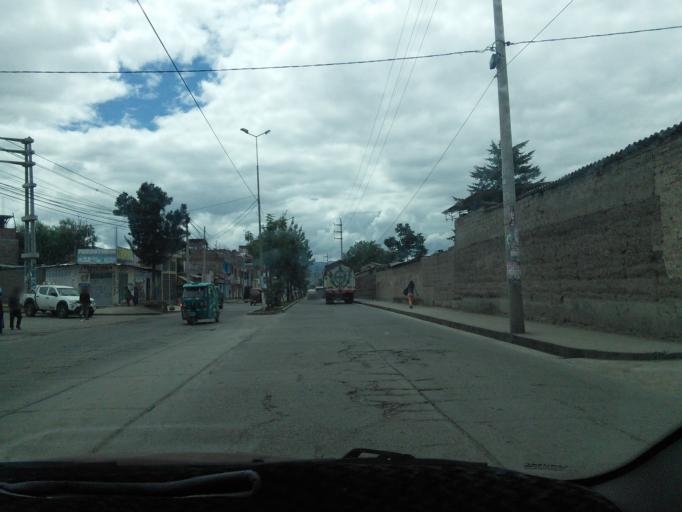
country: PE
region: Ayacucho
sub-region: Provincia de Huamanga
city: Ayacucho
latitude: -13.1538
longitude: -74.2230
